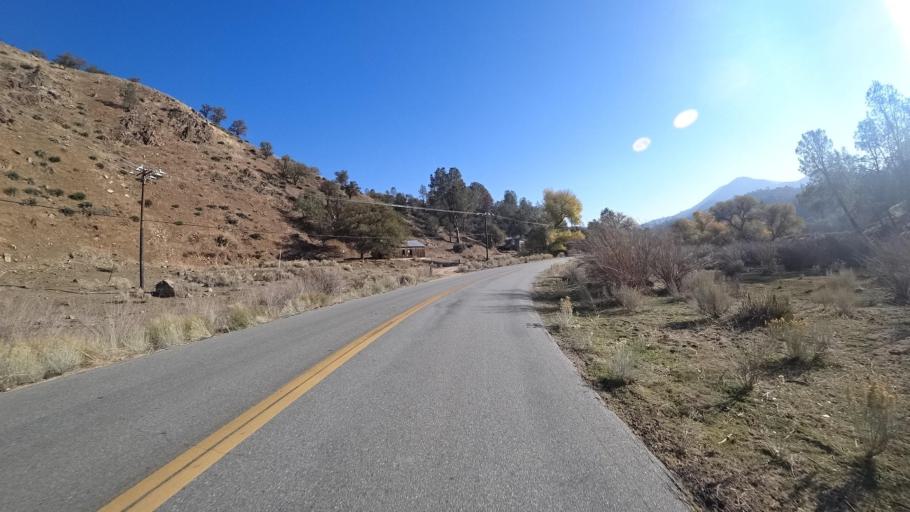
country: US
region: California
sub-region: Kern County
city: Golden Hills
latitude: 35.3075
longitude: -118.4292
